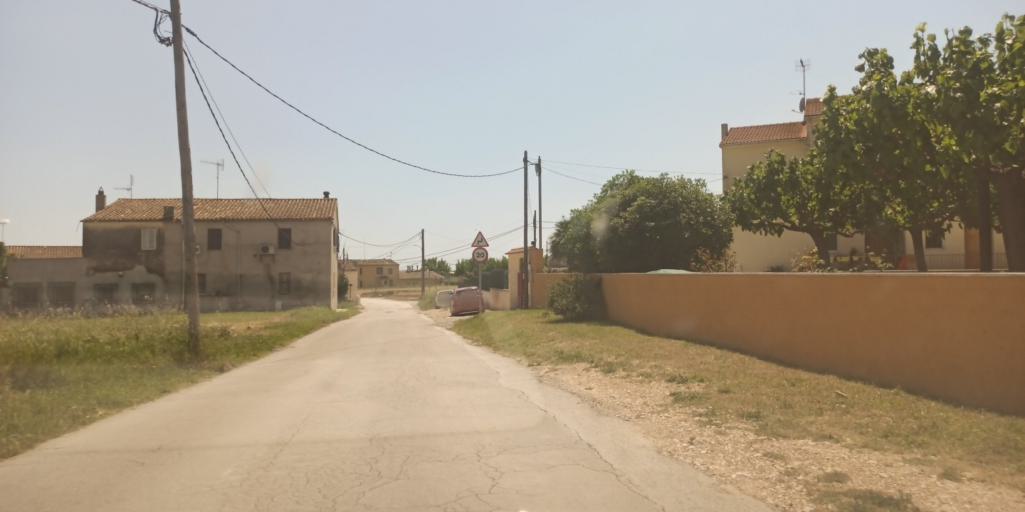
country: ES
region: Catalonia
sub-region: Provincia de Barcelona
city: Vilobi del Penedes
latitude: 41.3442
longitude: 1.6564
